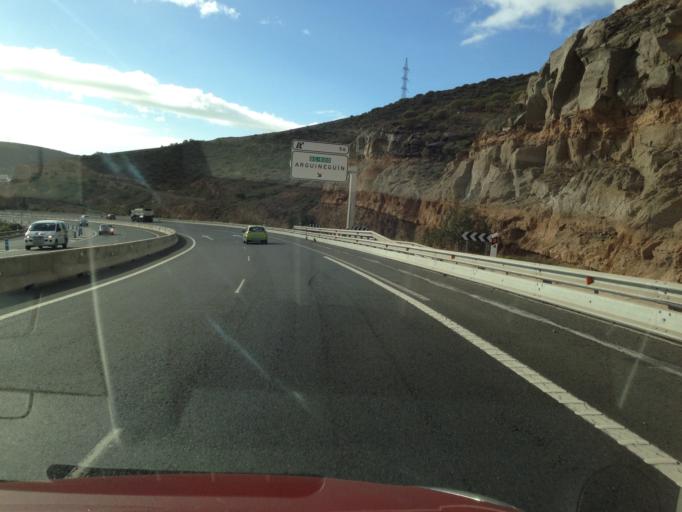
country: ES
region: Canary Islands
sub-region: Provincia de Las Palmas
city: Puerto Rico
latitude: 27.7682
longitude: -15.6748
